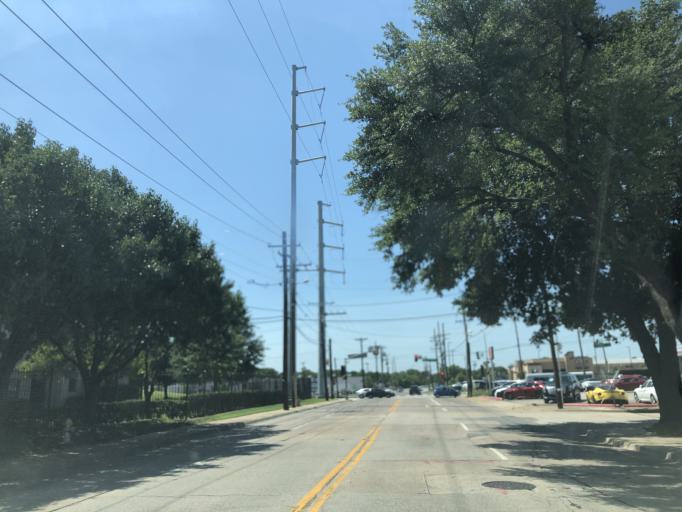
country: US
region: Texas
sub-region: Dallas County
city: University Park
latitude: 32.8274
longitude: -96.8437
